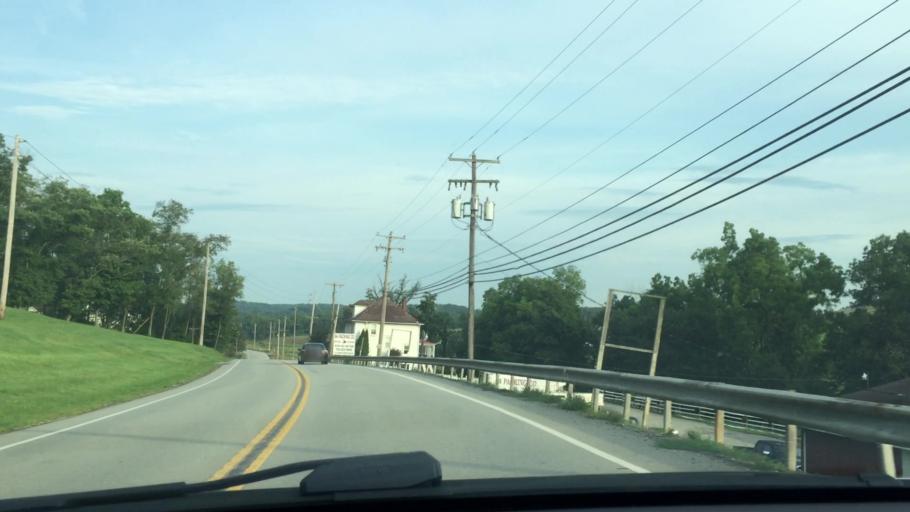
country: US
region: Pennsylvania
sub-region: Washington County
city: McMurray
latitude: 40.1799
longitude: -80.1190
